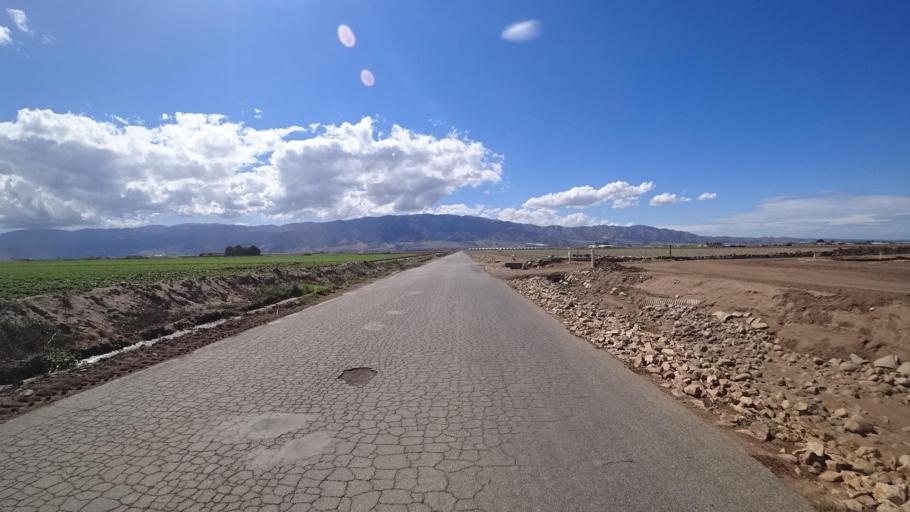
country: US
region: California
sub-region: Monterey County
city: Chualar
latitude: 36.5985
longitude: -121.5224
